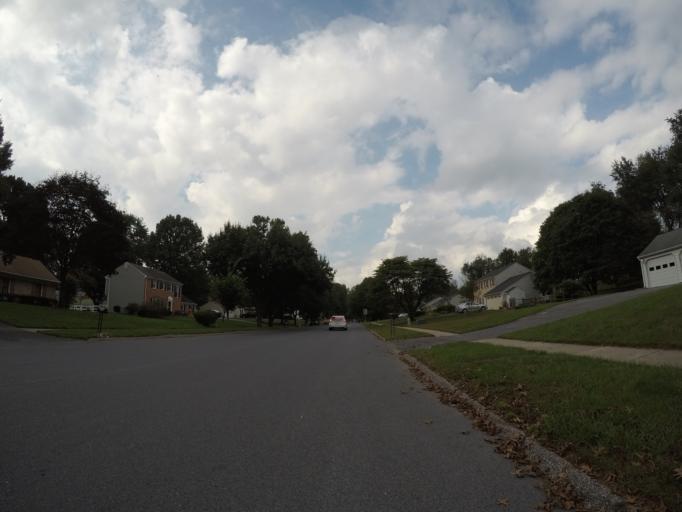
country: US
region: Maryland
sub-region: Howard County
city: Columbia
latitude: 39.2661
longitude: -76.8592
